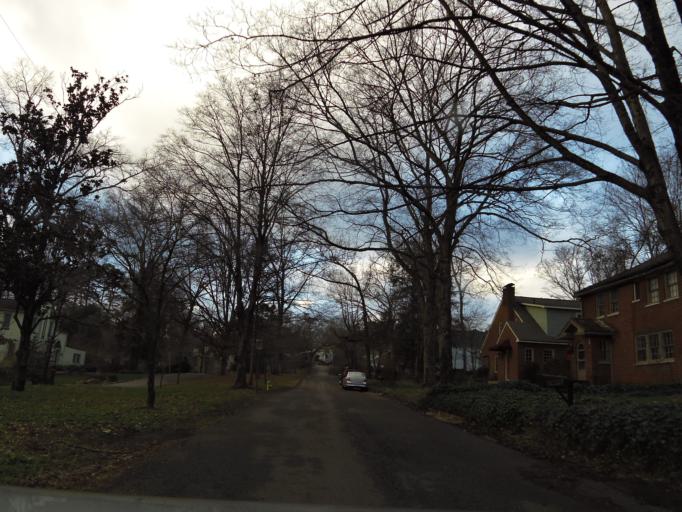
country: US
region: Tennessee
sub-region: Knox County
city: Knoxville
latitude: 36.0050
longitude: -83.8997
